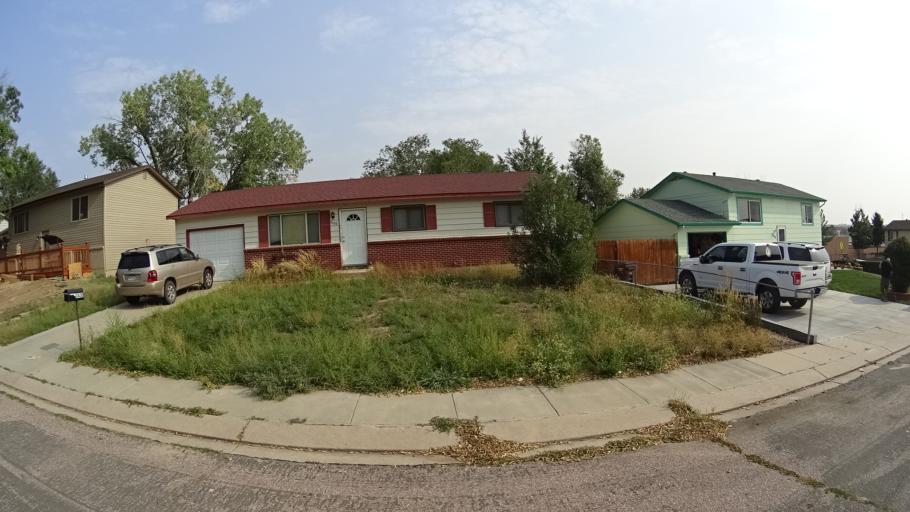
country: US
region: Colorado
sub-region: El Paso County
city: Stratmoor
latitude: 38.8039
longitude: -104.7642
